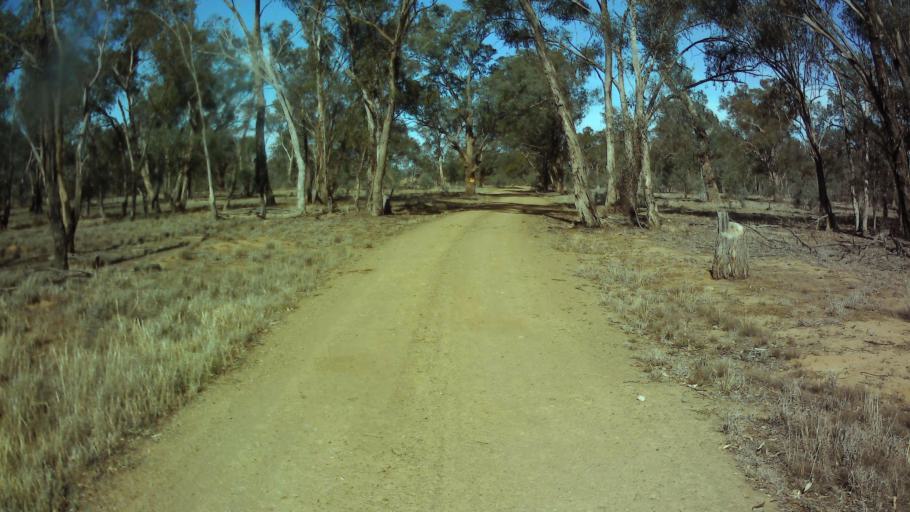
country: AU
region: New South Wales
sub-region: Weddin
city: Grenfell
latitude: -33.7337
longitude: 148.0901
